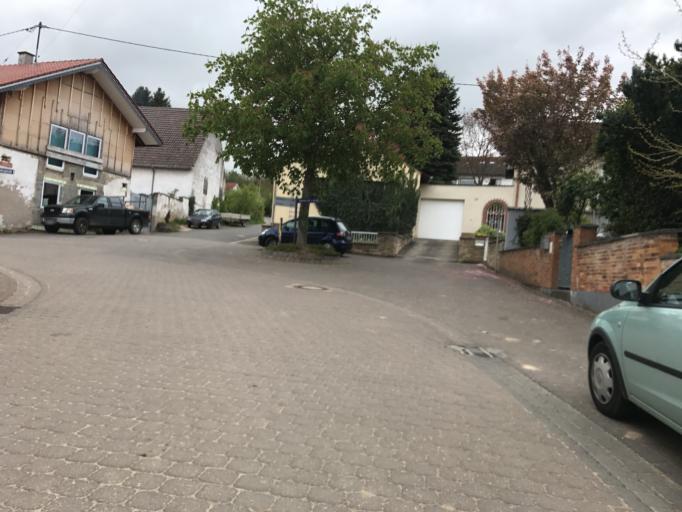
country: DE
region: Rheinland-Pfalz
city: Engelstadt
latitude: 49.9035
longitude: 8.0683
